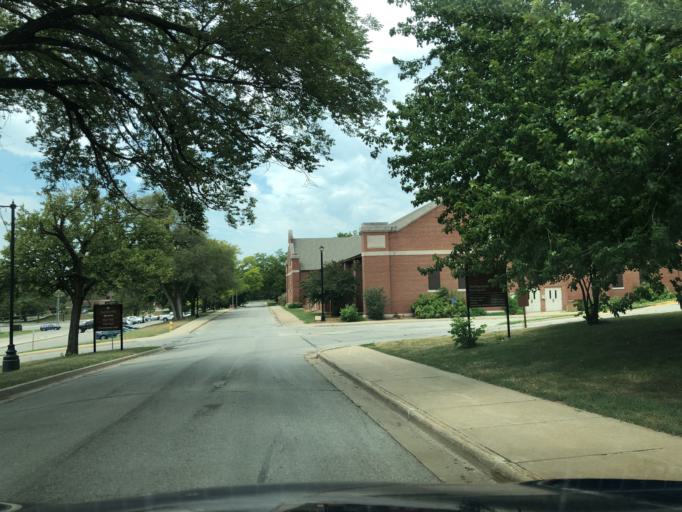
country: US
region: Kansas
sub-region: Leavenworth County
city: Leavenworth
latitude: 39.3488
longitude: -94.9147
